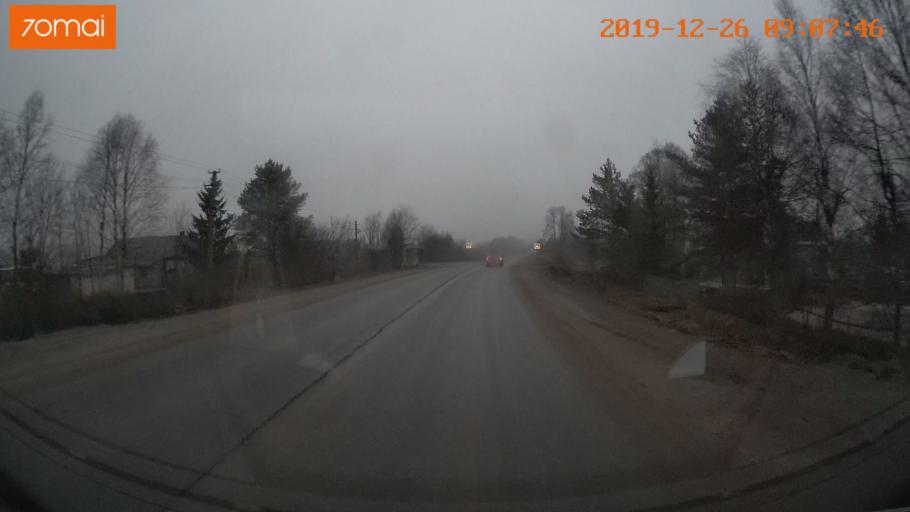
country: RU
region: Vologda
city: Gryazovets
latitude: 58.8496
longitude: 40.2468
